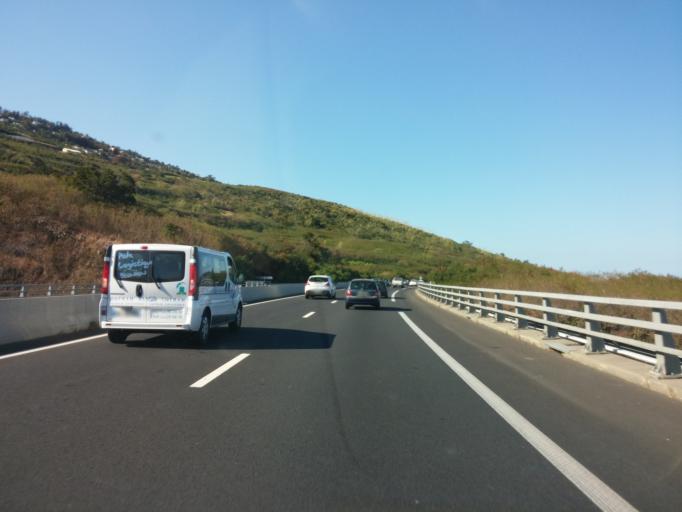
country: RE
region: Reunion
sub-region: Reunion
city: Trois-Bassins
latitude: -21.1324
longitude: 55.2841
